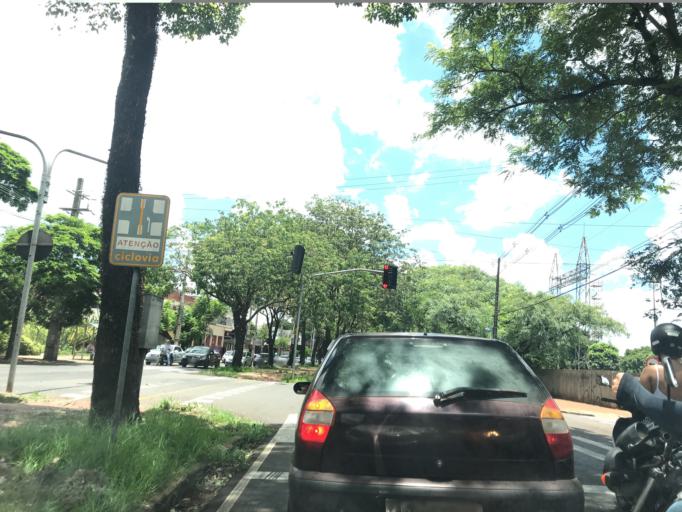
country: BR
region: Parana
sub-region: Maringa
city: Maringa
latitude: -23.4064
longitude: -51.9226
